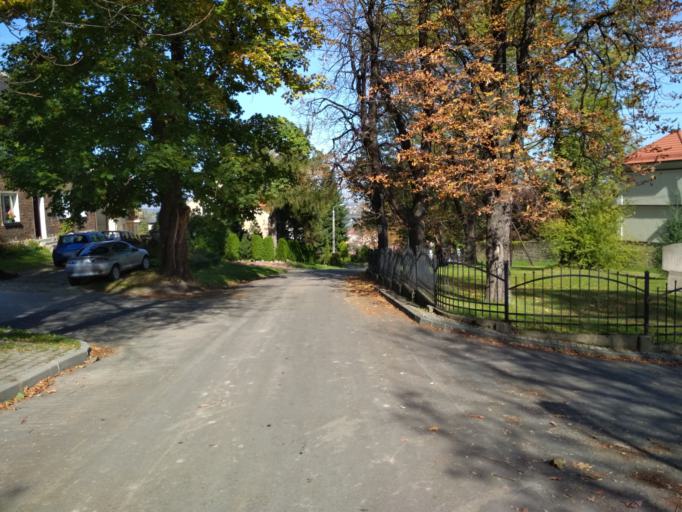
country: PL
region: Lesser Poland Voivodeship
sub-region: Powiat wadowicki
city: Kalwaria Zebrzydowska
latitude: 49.8607
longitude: 19.6740
